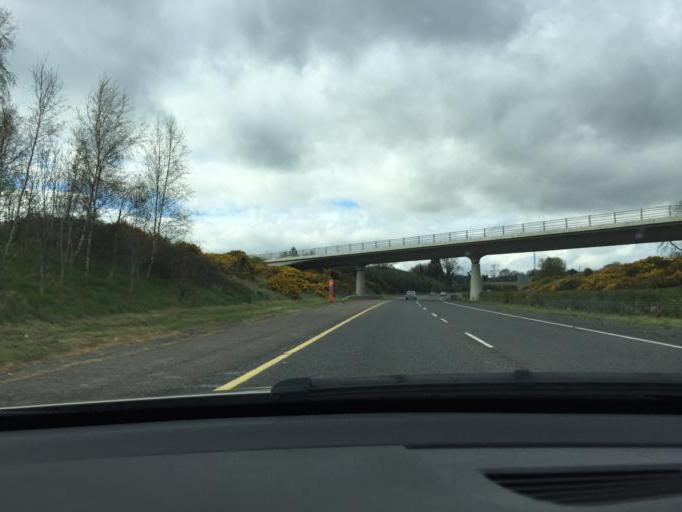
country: IE
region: Leinster
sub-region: Wicklow
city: Ashford
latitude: 53.0092
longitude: -6.0960
